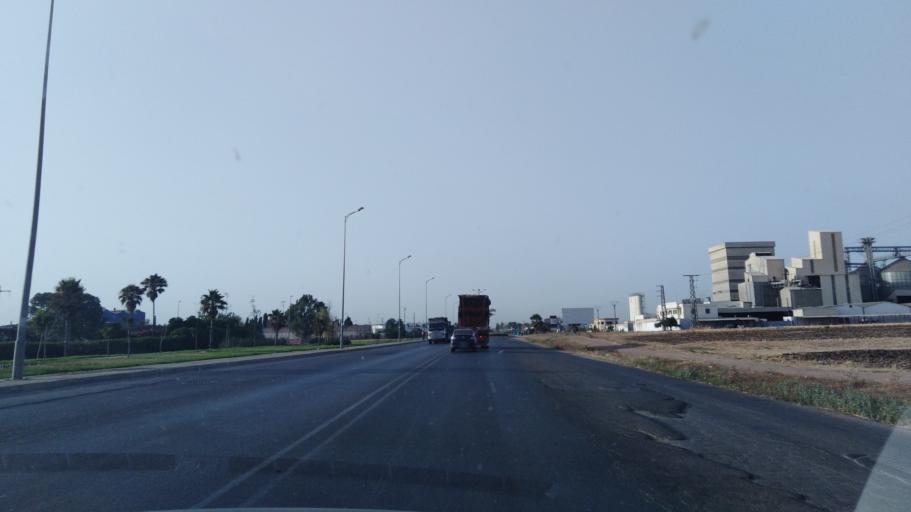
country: MA
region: Chaouia-Ouardigha
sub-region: Settat Province
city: Berrechid
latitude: 33.2374
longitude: -7.5885
